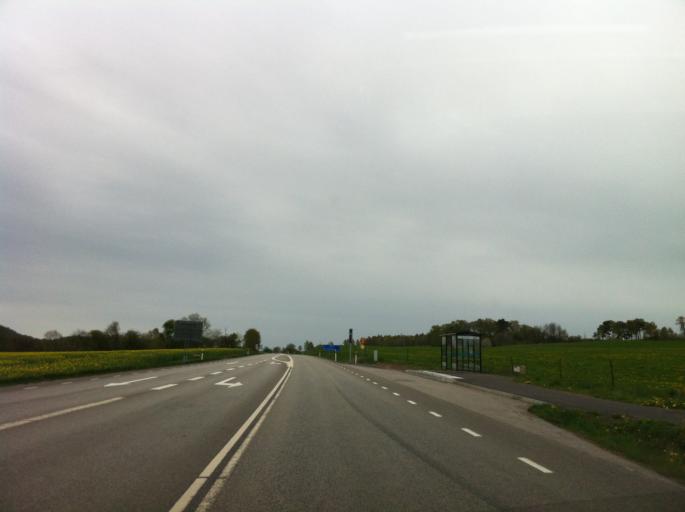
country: SE
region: Halland
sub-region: Falkenbergs Kommun
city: Falkenberg
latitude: 56.9811
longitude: 12.5786
